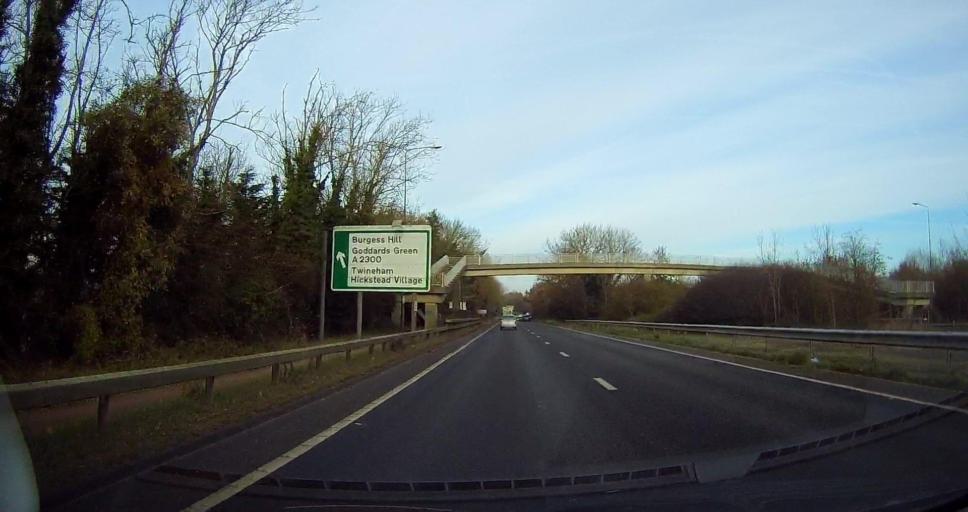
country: GB
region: England
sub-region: West Sussex
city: Hurstpierpoint
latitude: 50.9612
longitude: -0.1939
